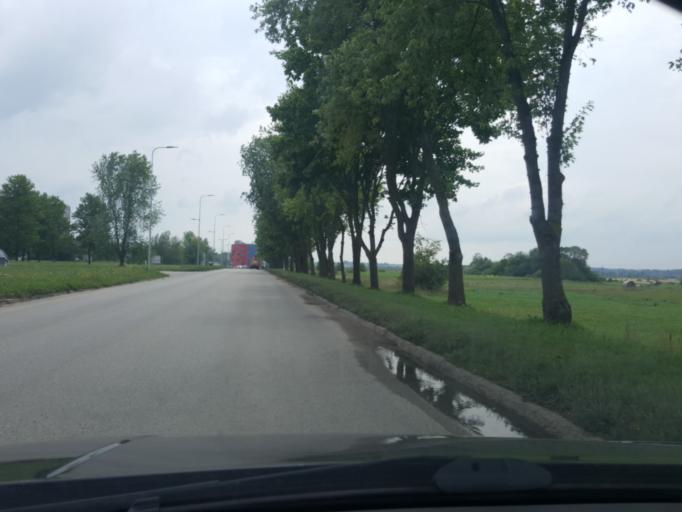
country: LT
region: Alytaus apskritis
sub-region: Alytus
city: Alytus
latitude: 54.4323
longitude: 24.0033
